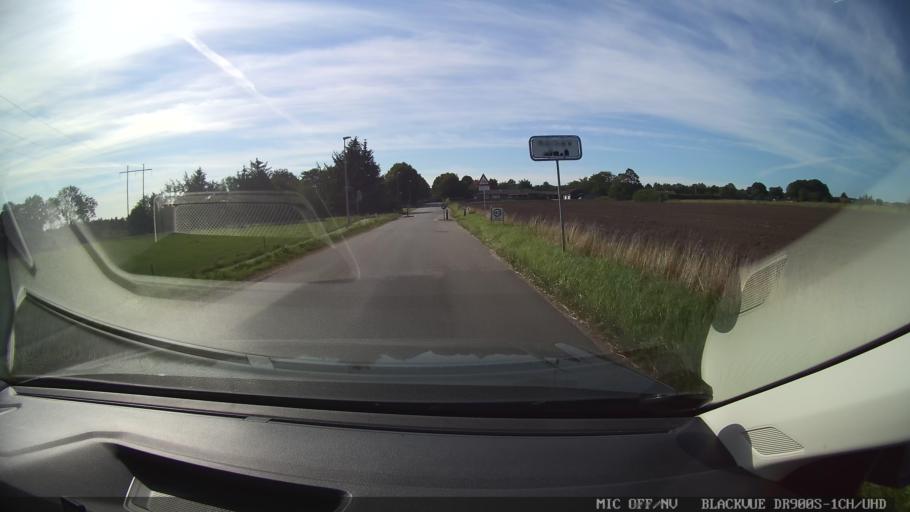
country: DK
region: North Denmark
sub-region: Mariagerfjord Kommune
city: Hobro
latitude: 56.5416
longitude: 9.8267
